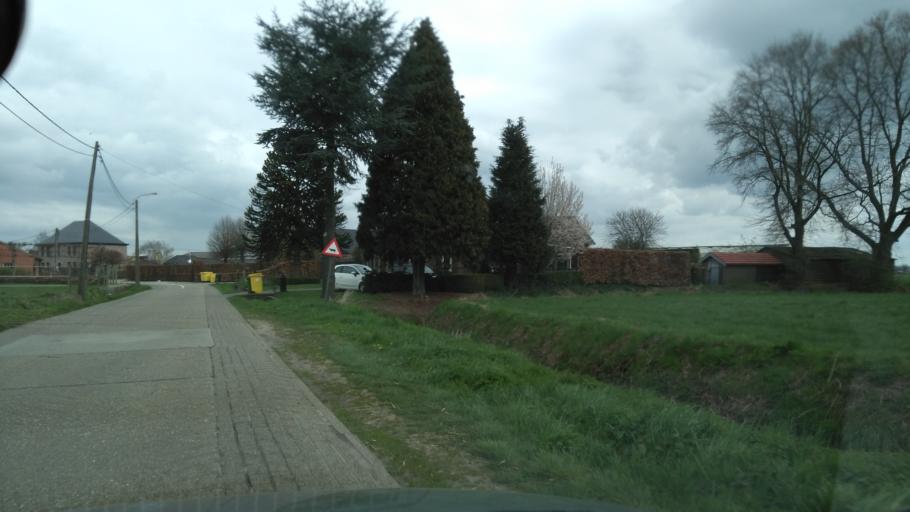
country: BE
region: Flanders
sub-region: Provincie Antwerpen
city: Ravels
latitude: 51.4081
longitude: 4.9844
